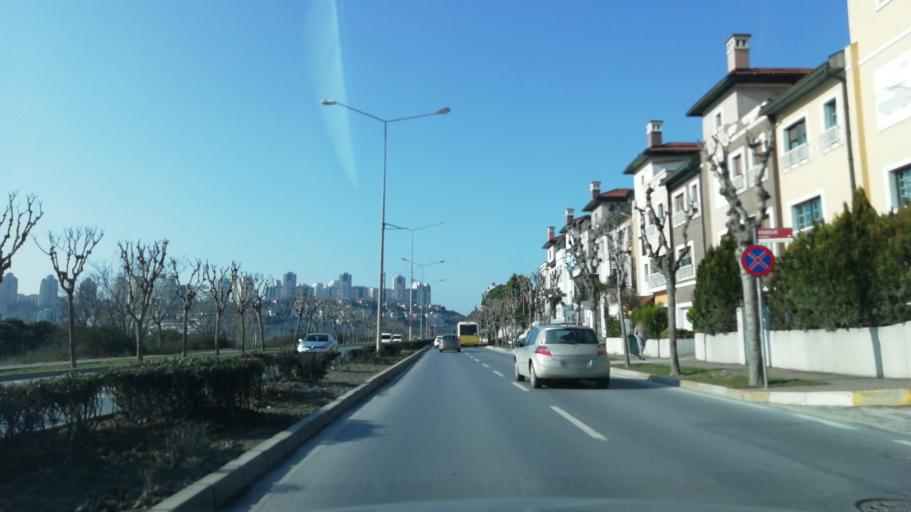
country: TR
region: Istanbul
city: Esenyurt
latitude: 41.0662
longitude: 28.6978
